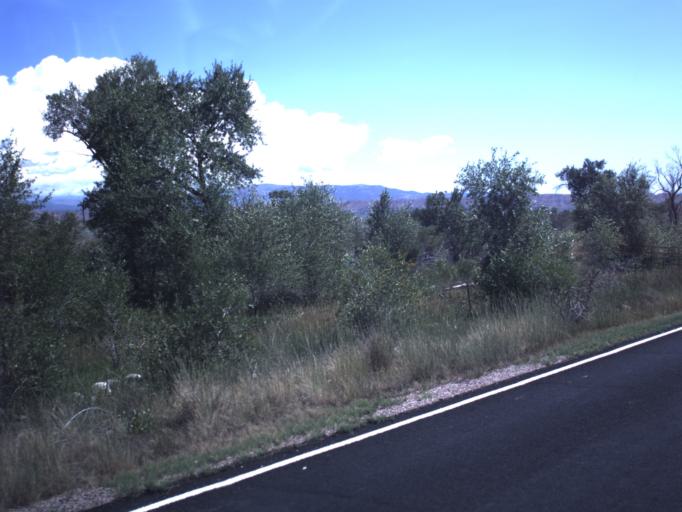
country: US
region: Utah
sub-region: Duchesne County
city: Roosevelt
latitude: 40.4037
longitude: -109.8803
